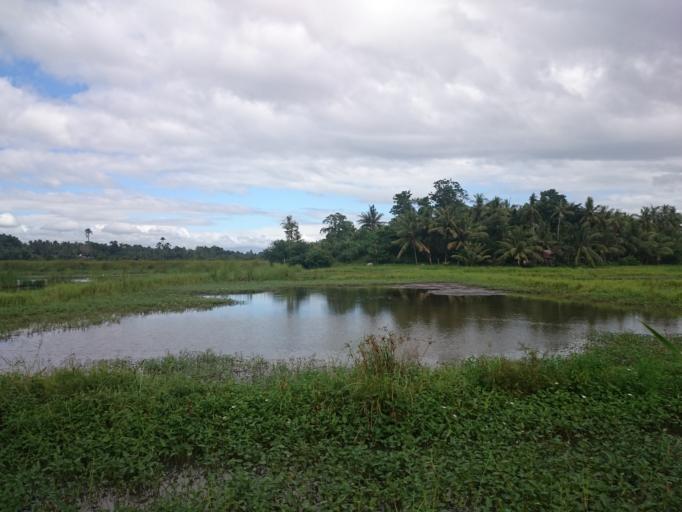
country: PH
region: Central Visayas
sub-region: Province of Negros Oriental
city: Tanjay
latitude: 9.5013
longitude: 123.1545
